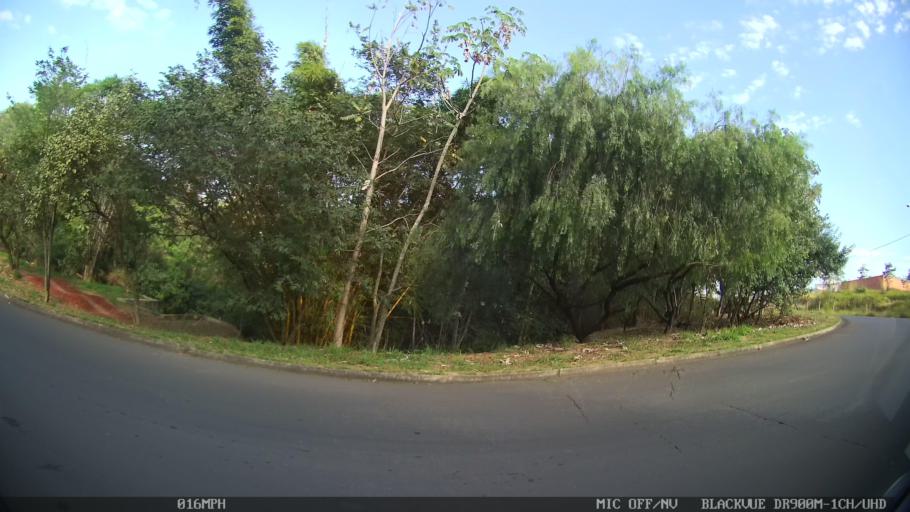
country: BR
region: Sao Paulo
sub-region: Americana
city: Americana
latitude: -22.7348
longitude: -47.3432
